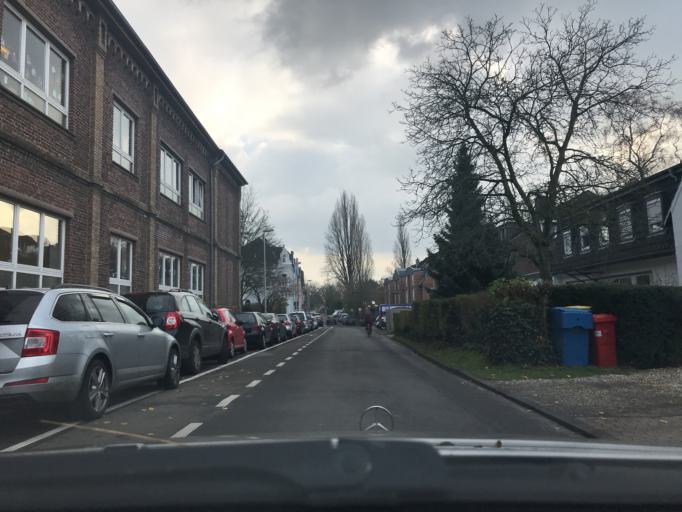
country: DE
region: North Rhine-Westphalia
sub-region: Regierungsbezirk Dusseldorf
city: Krefeld
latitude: 51.3468
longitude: 6.6123
